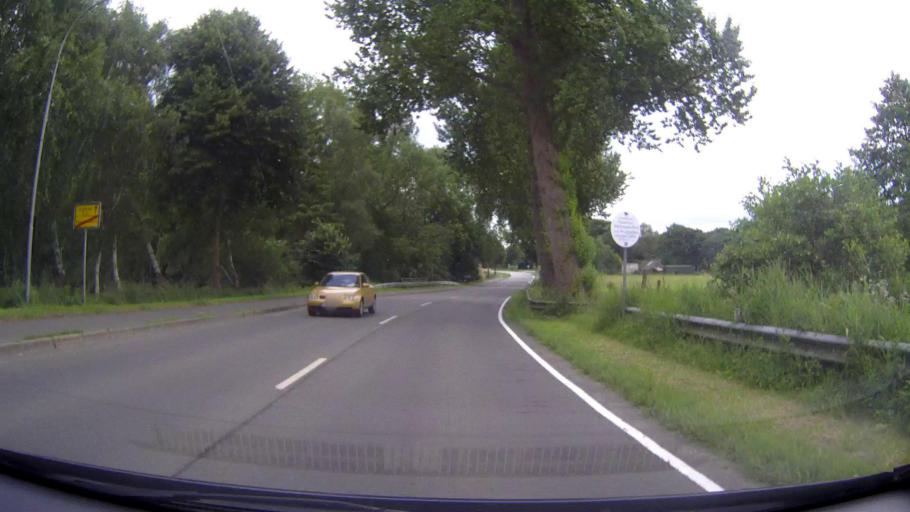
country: DE
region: Schleswig-Holstein
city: Gokels
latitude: 54.1196
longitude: 9.4461
